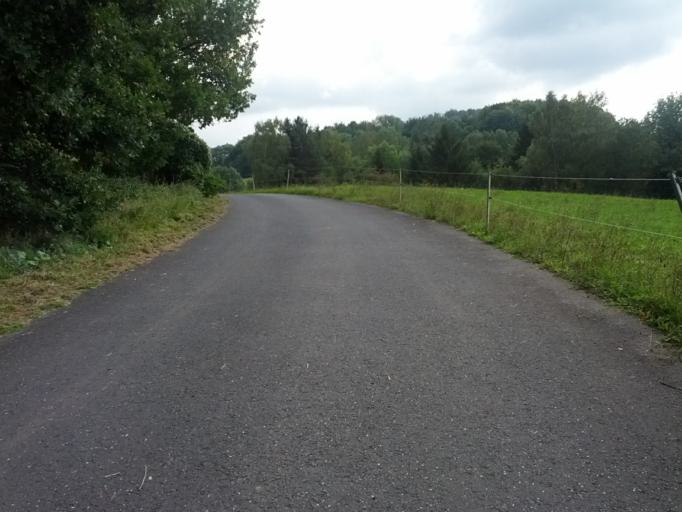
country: DE
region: Thuringia
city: Thal
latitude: 50.9327
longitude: 10.3974
